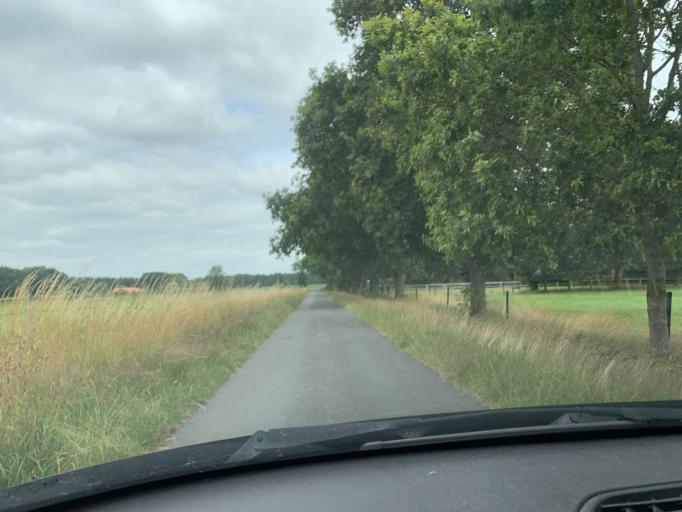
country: DE
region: Lower Saxony
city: Westerstede
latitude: 53.2584
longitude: 7.9742
